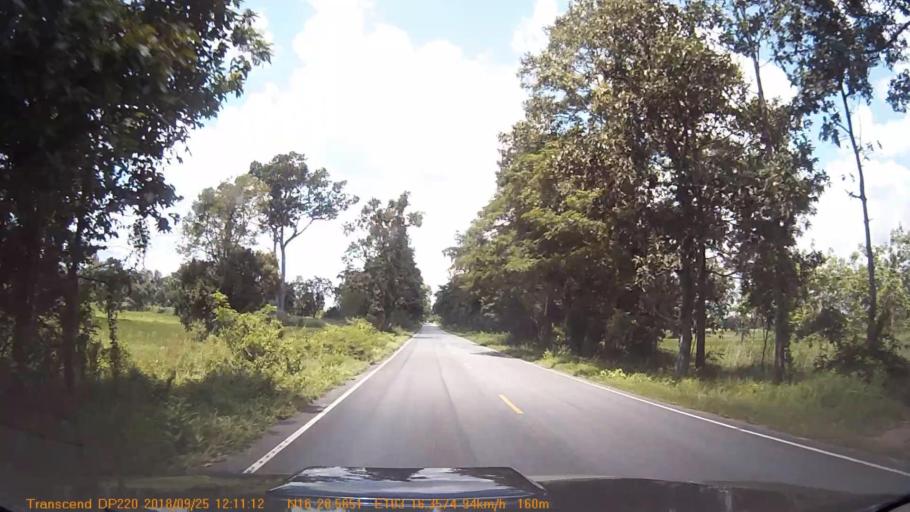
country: TH
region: Kalasin
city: Huai Mek
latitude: 16.4762
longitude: 103.2725
